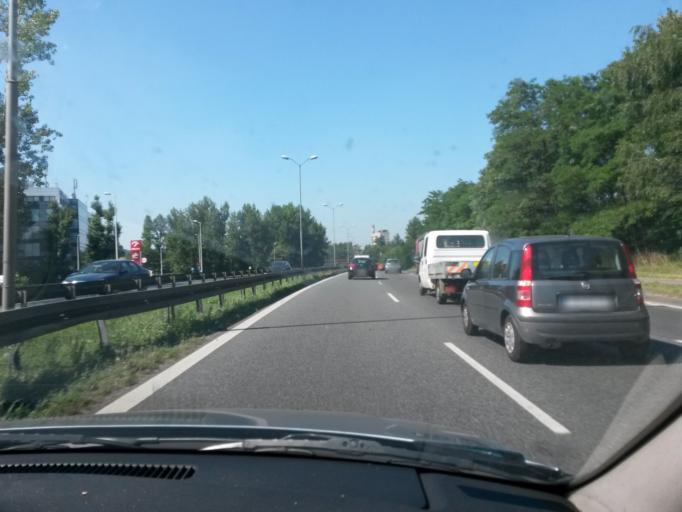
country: PL
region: Silesian Voivodeship
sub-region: Katowice
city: Katowice
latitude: 50.2543
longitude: 19.0479
